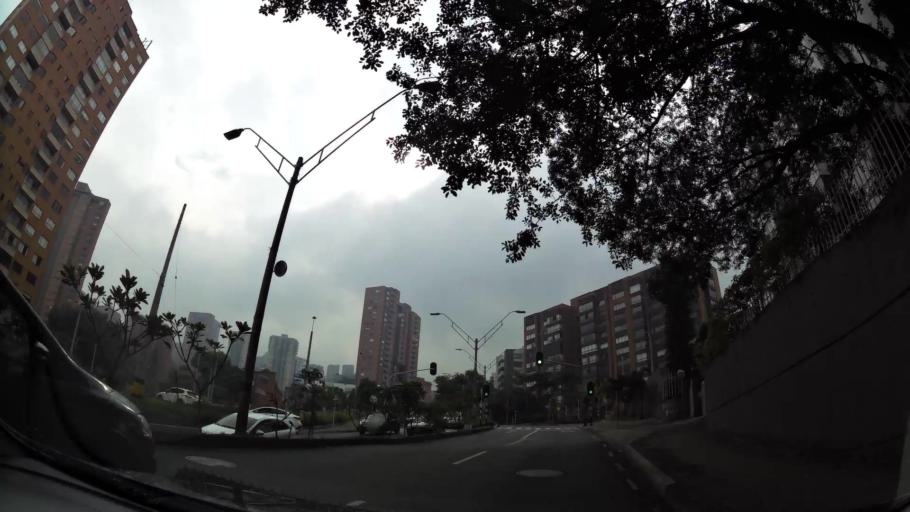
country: CO
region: Antioquia
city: Envigado
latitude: 6.1919
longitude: -75.5680
